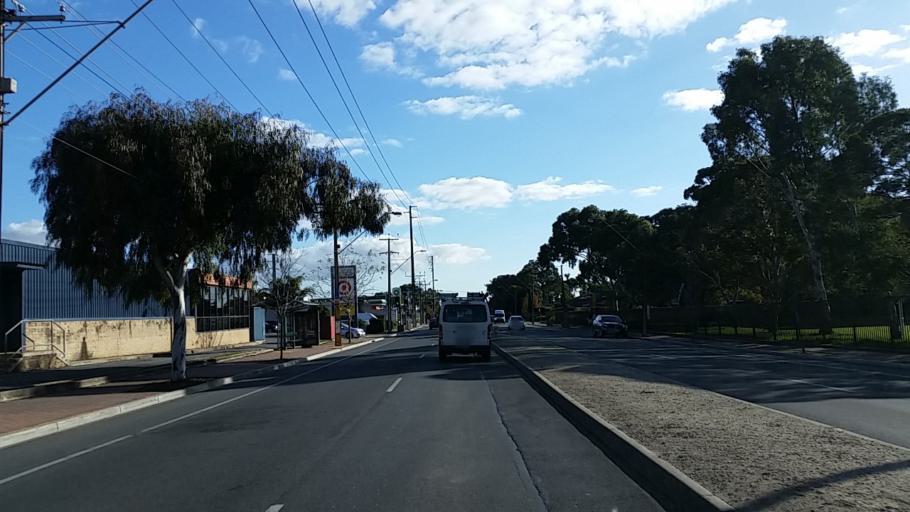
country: AU
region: South Australia
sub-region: Campbelltown
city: Paradise
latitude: -34.8763
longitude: 138.6755
